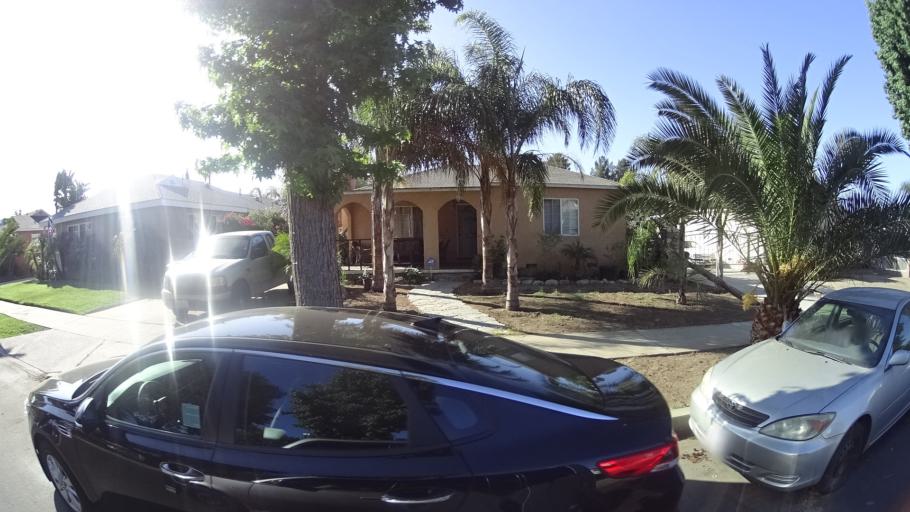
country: US
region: California
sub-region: Los Angeles County
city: Van Nuys
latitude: 34.2274
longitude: -118.4258
